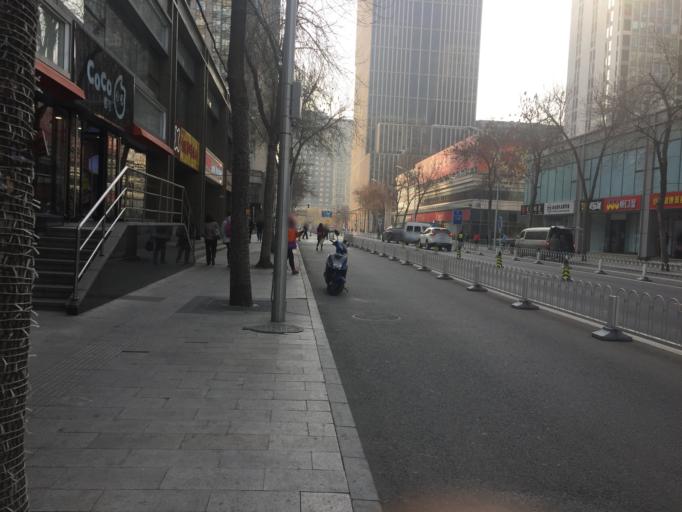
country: CN
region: Beijing
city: Chaowai
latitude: 39.9102
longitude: 116.4656
